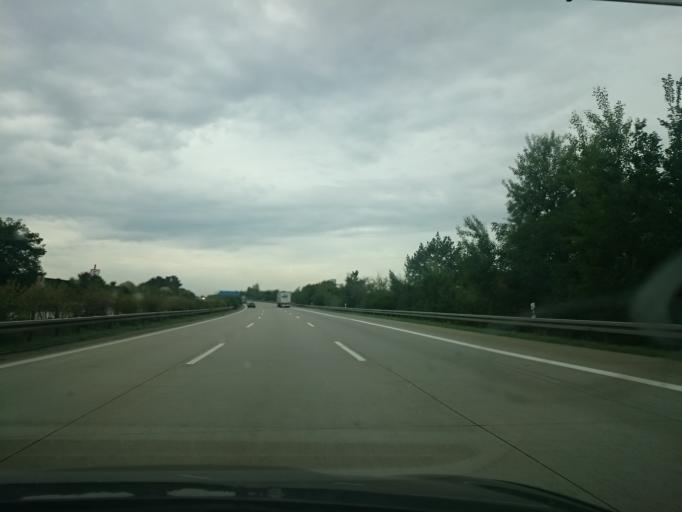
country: DE
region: Brandenburg
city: Linthe
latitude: 52.1628
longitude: 12.7874
